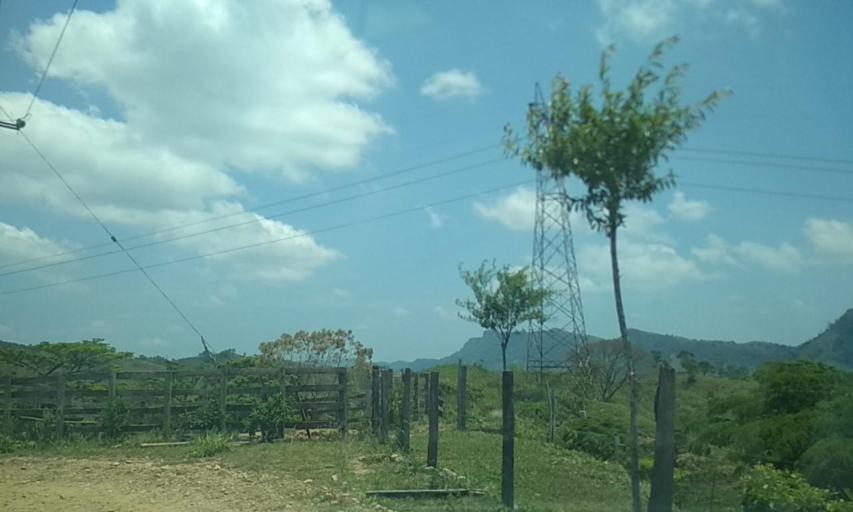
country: MX
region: Chiapas
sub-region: Tecpatan
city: Raudales Malpaso
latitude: 17.3981
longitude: -93.7462
